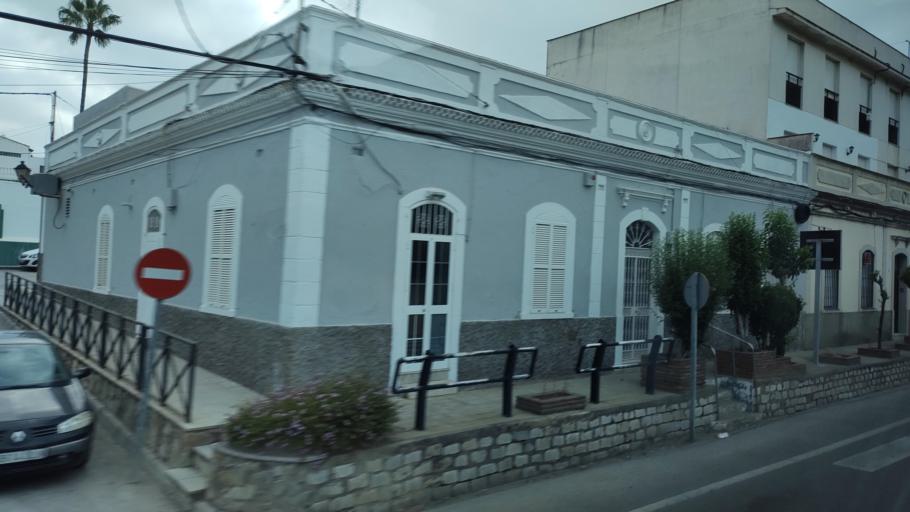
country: ES
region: Andalusia
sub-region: Provincia de Cadiz
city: San Roque
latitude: 36.1791
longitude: -5.3787
